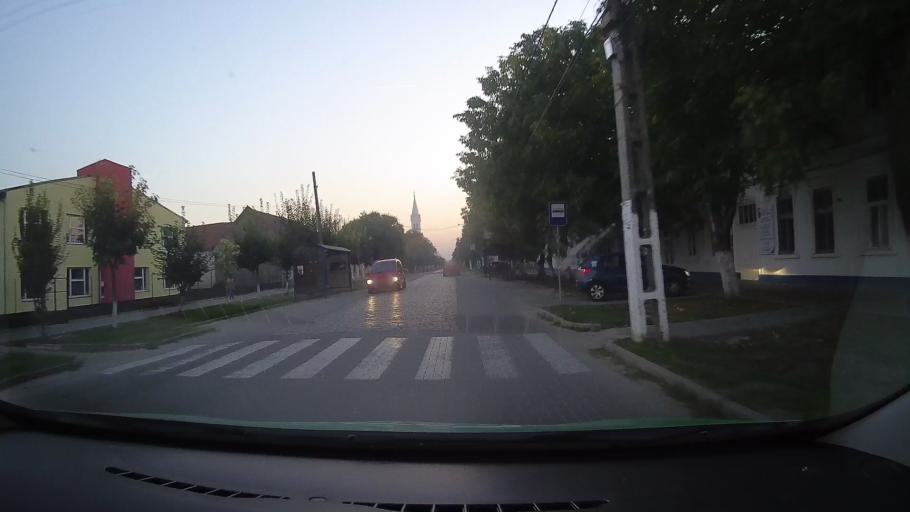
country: RO
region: Arad
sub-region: Comuna Santana
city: Santana
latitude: 46.3437
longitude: 21.4994
